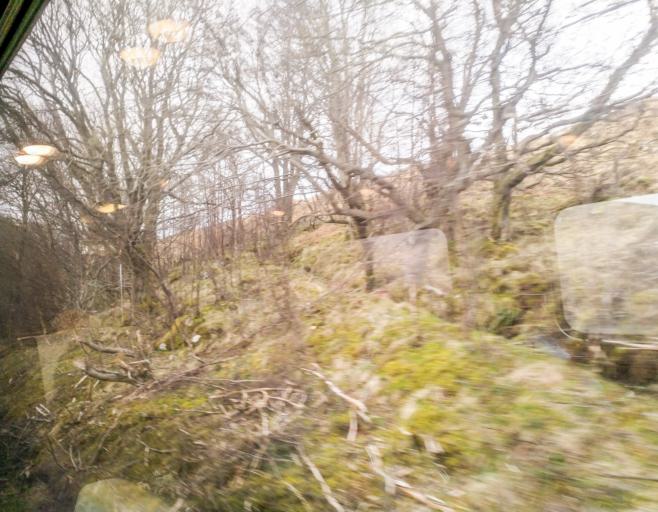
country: GB
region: Scotland
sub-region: Highland
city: Spean Bridge
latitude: 56.7833
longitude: -4.7325
